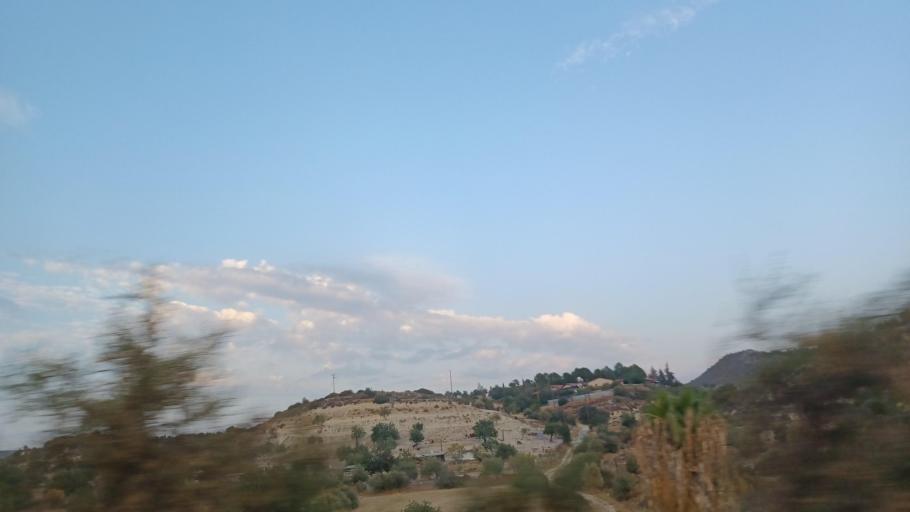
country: CY
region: Limassol
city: Pano Polemidia
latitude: 34.7527
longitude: 32.9732
